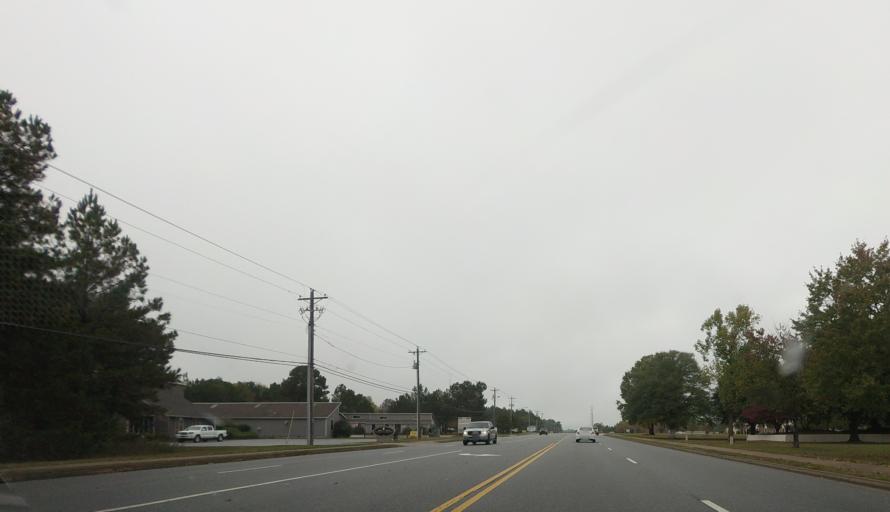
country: US
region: Georgia
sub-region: Houston County
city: Centerville
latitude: 32.5961
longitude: -83.6651
